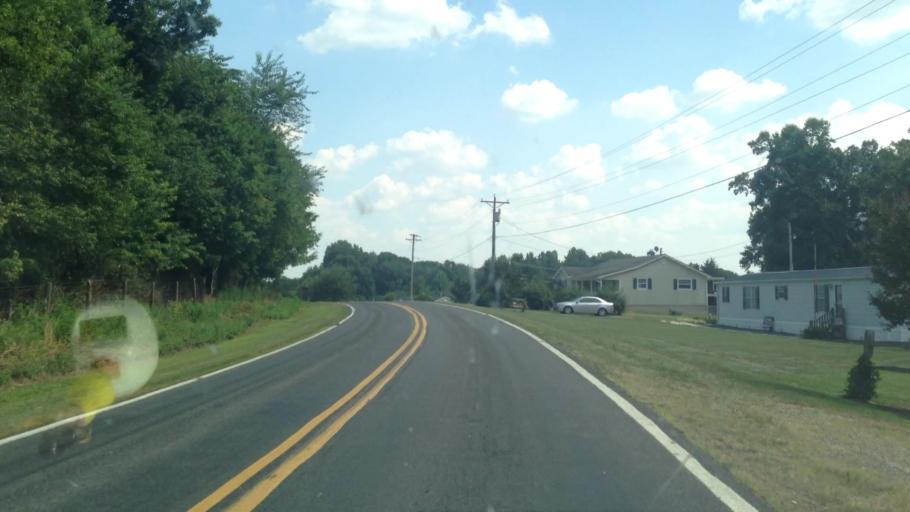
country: US
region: North Carolina
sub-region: Forsyth County
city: Walkertown
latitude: 36.2250
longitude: -80.1177
